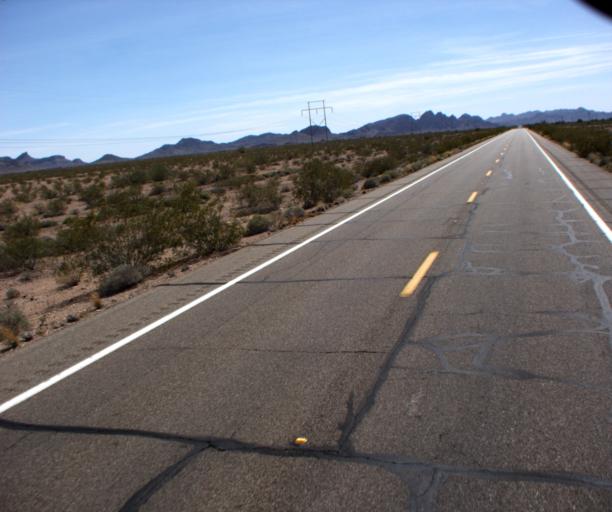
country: US
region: Arizona
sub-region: La Paz County
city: Quartzsite
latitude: 33.3611
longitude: -114.2171
